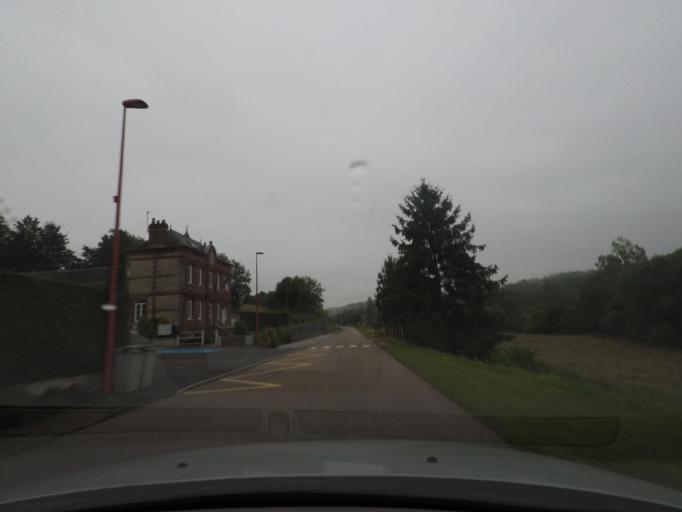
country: FR
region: Haute-Normandie
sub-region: Departement de la Seine-Maritime
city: Fontaine-le-Bourg
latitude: 49.5782
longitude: 1.2055
